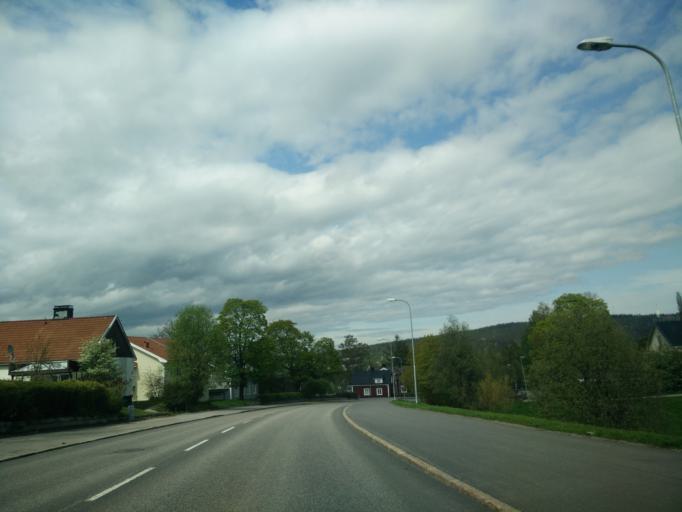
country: SE
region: Vaesternorrland
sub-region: Sundsvalls Kommun
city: Sundsvall
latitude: 62.3833
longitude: 17.2822
